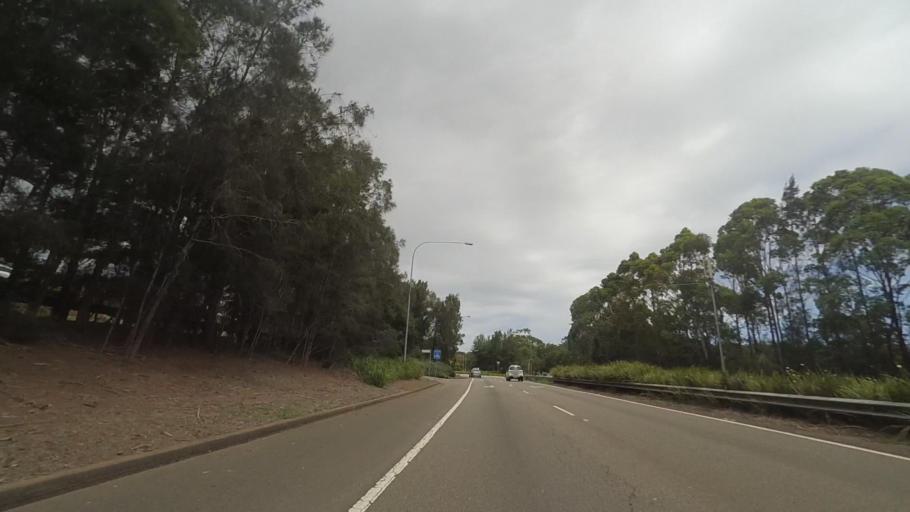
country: AU
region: New South Wales
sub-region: Wyong Shire
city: Berkeley Vale
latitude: -33.3505
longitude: 151.4326
